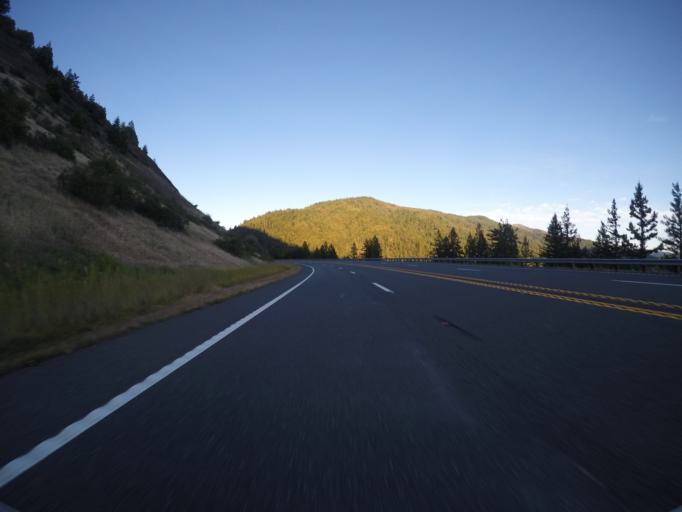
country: US
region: California
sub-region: Mendocino County
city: Laytonville
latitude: 39.8288
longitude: -123.6569
